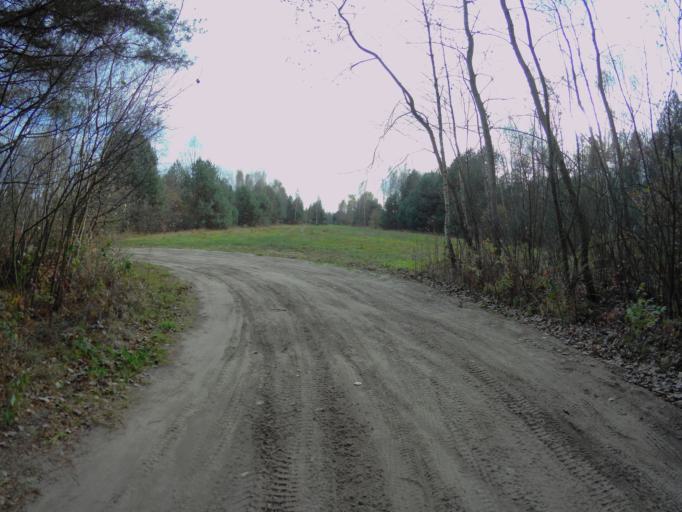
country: PL
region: Subcarpathian Voivodeship
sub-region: Powiat kolbuszowski
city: Lipnica
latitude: 50.3259
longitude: 21.9368
